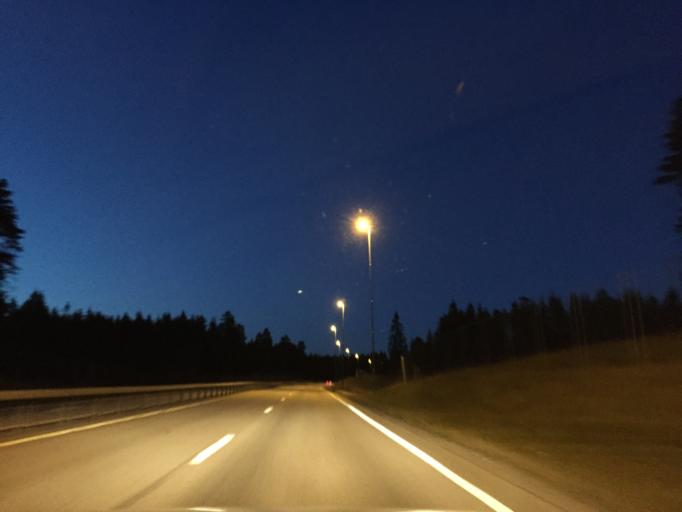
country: NO
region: Akershus
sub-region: Nes
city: Neskollen
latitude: 60.1110
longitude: 11.2670
